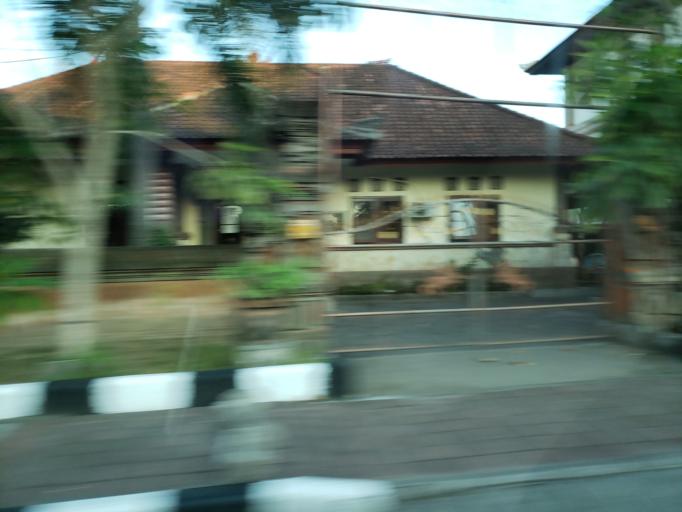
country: ID
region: Bali
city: Kelanabian
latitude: -8.7639
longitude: 115.1787
